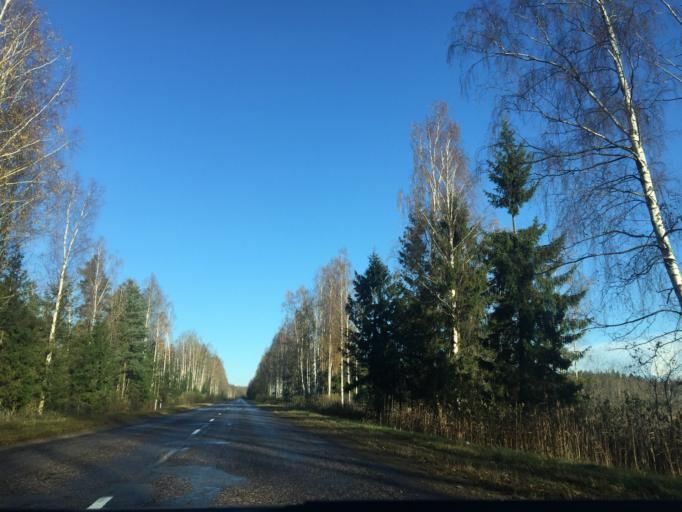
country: LV
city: Tireli
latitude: 56.9076
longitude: 23.5279
